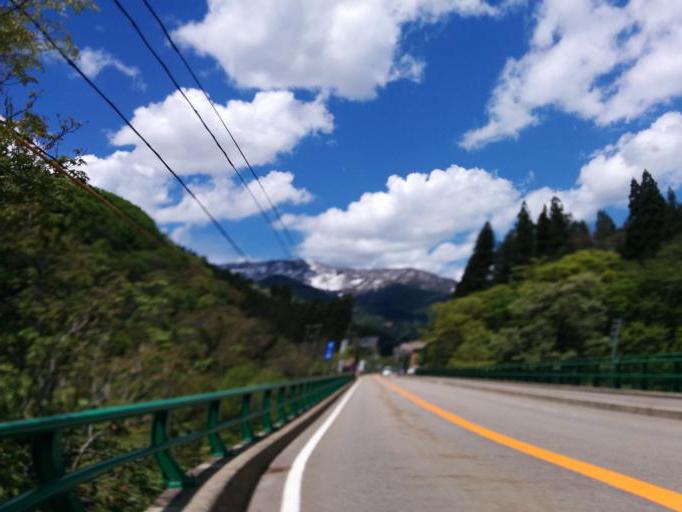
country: JP
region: Toyama
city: Fukumitsu
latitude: 36.3608
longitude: 136.8743
